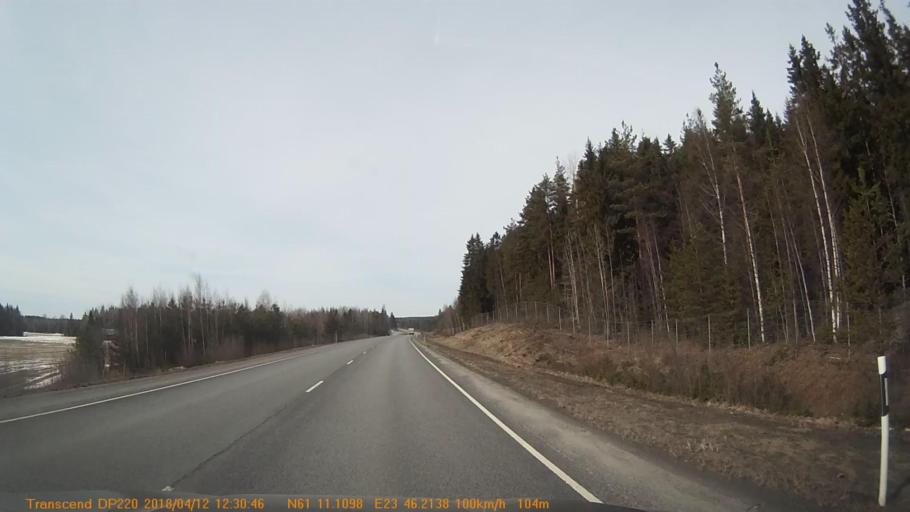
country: FI
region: Pirkanmaa
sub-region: Etelae-Pirkanmaa
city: Viiala
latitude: 61.1852
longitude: 23.7697
